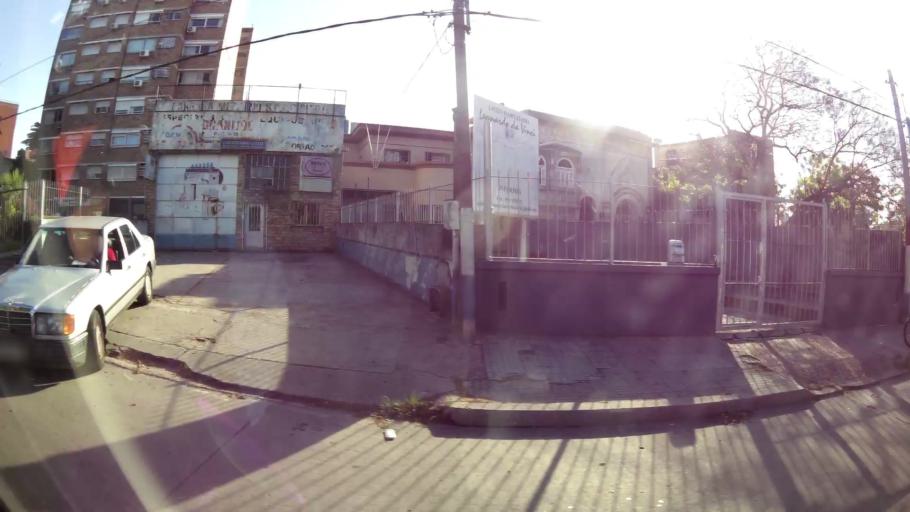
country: UY
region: Montevideo
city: Montevideo
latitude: -34.8784
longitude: -56.1560
